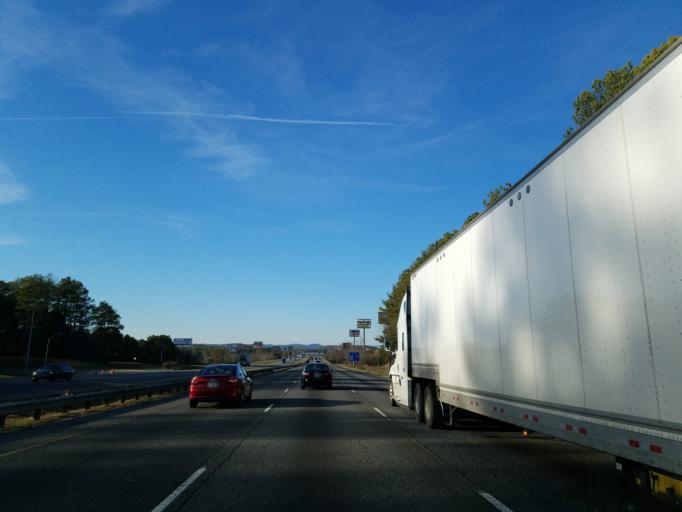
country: US
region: Georgia
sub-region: Gordon County
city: Calhoun
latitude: 34.5627
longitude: -84.9408
